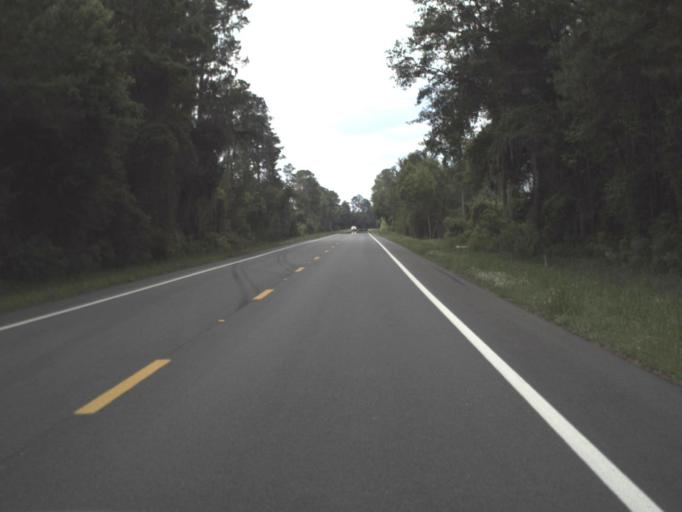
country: US
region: Florida
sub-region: Hamilton County
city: Jasper
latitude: 30.5319
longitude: -82.6761
